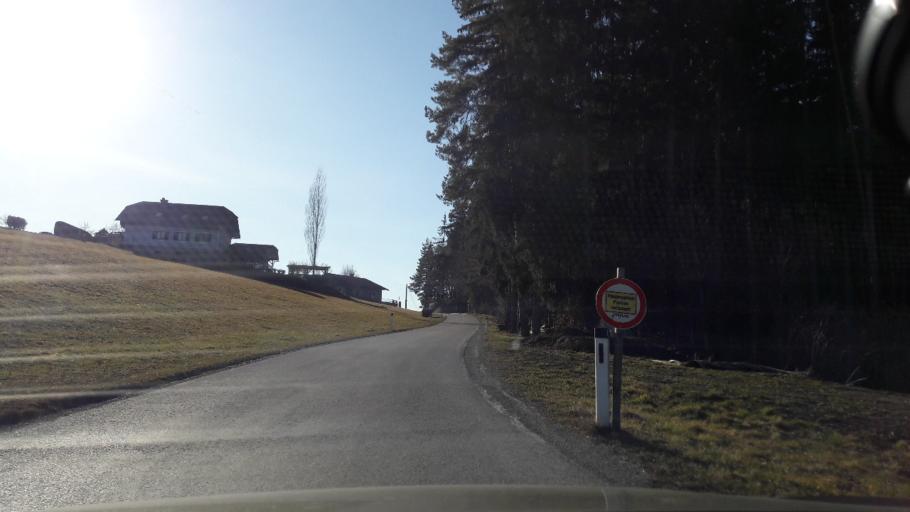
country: AT
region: Styria
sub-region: Politischer Bezirk Graz-Umgebung
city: Eisbach
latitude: 47.1151
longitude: 15.2819
